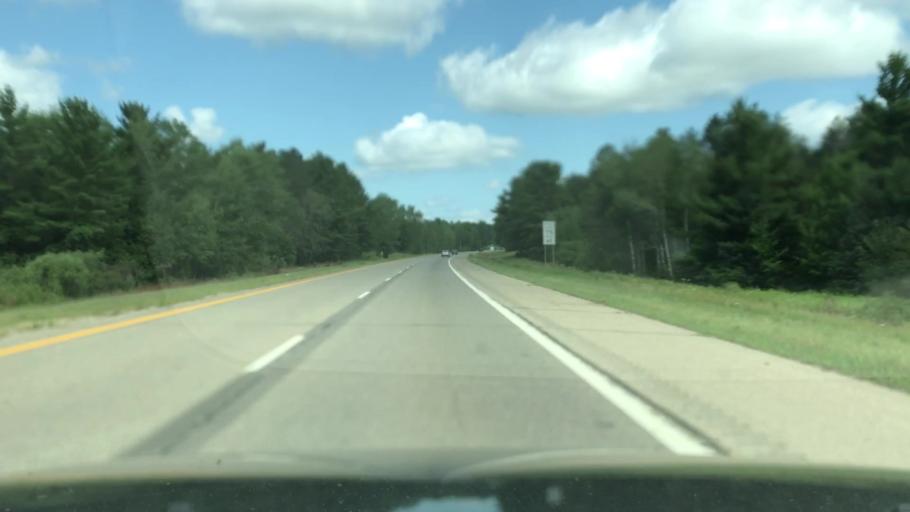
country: US
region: Michigan
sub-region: Mecosta County
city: Big Rapids
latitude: 43.6965
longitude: -85.5255
